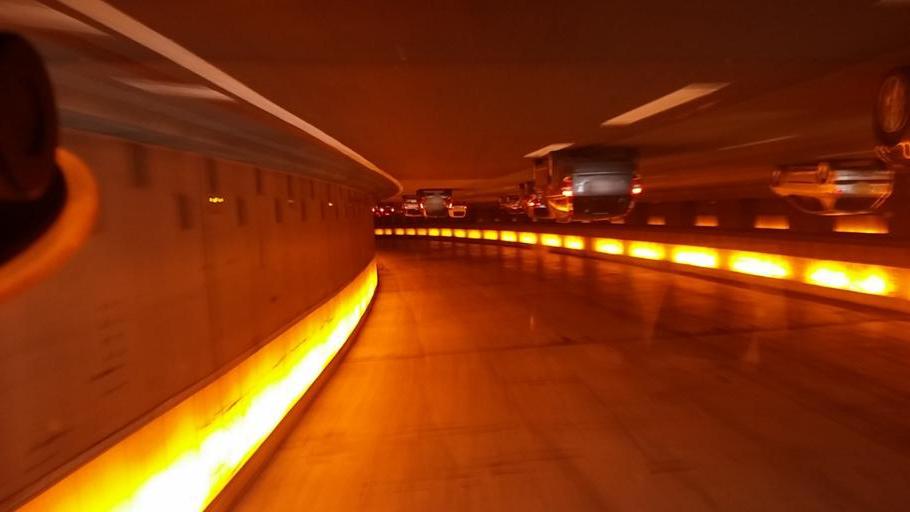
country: FR
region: Ile-de-France
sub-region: Departement des Hauts-de-Seine
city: Boulogne-Billancourt
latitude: 48.8512
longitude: 2.2524
